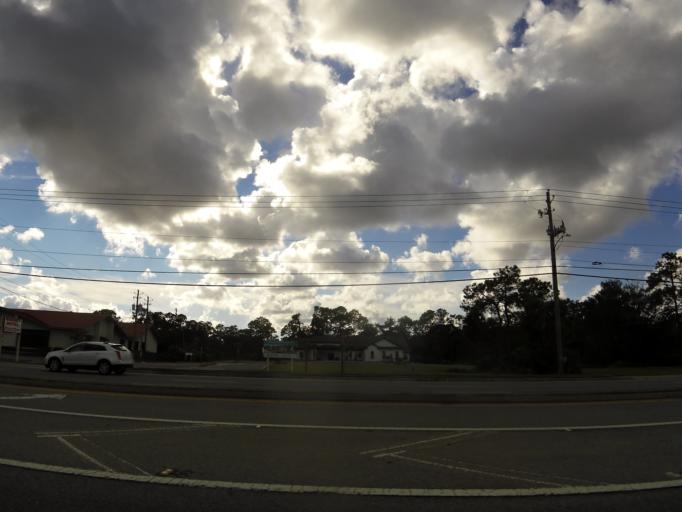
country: US
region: Georgia
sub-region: Glynn County
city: Brunswick
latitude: 31.1770
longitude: -81.4732
